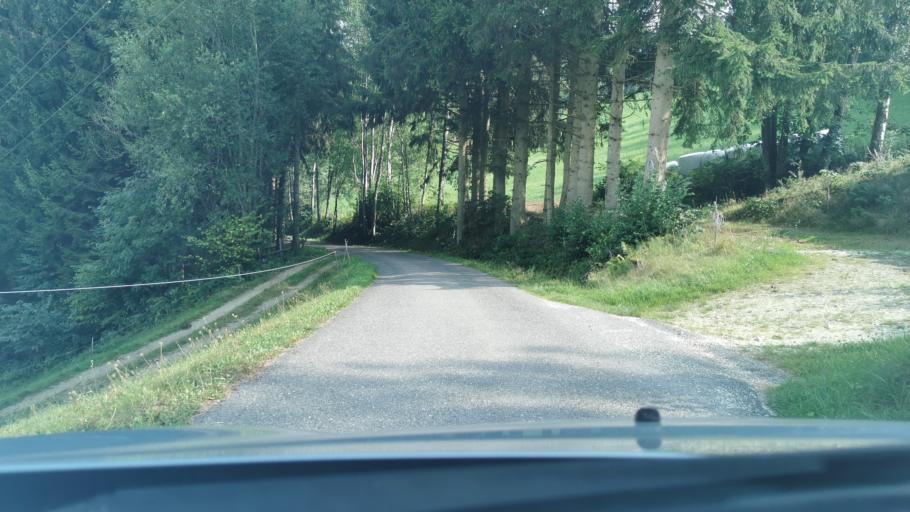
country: AT
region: Styria
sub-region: Politischer Bezirk Weiz
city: Strallegg
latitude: 47.4021
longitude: 15.6950
